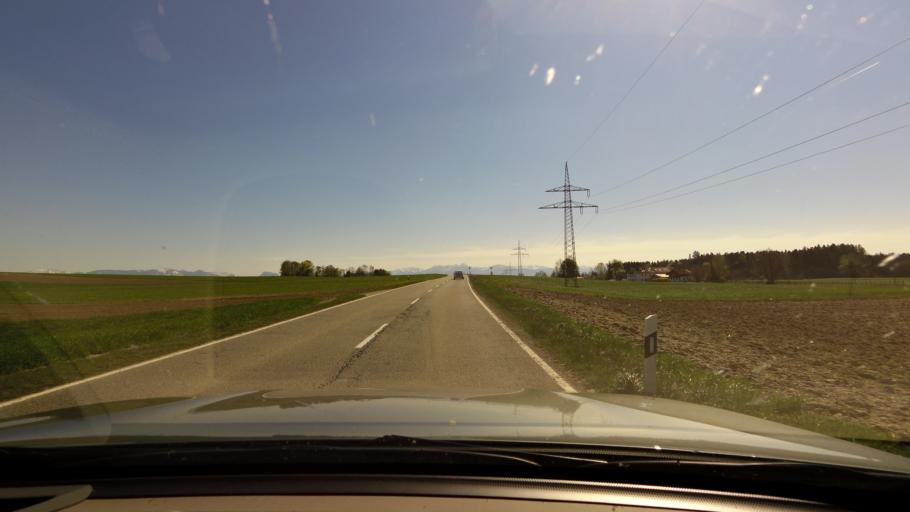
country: DE
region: Bavaria
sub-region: Upper Bavaria
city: Griesstatt
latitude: 47.9757
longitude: 12.1769
